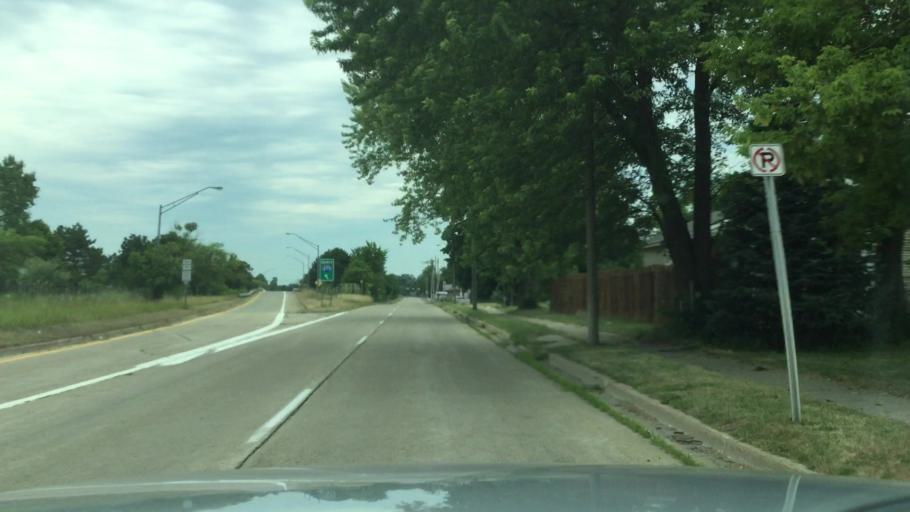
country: US
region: Michigan
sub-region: Genesee County
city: Beecher
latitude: 43.0698
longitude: -83.6825
